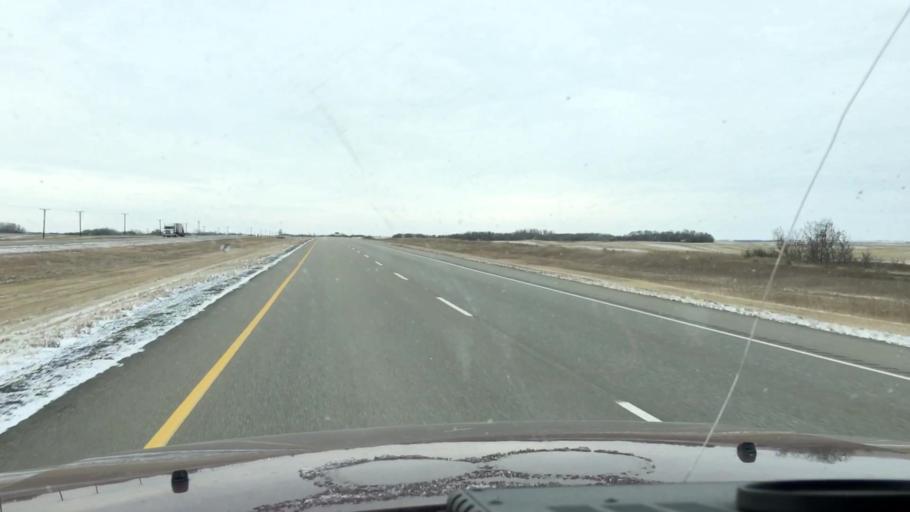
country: CA
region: Saskatchewan
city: Watrous
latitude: 51.3942
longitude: -106.1711
